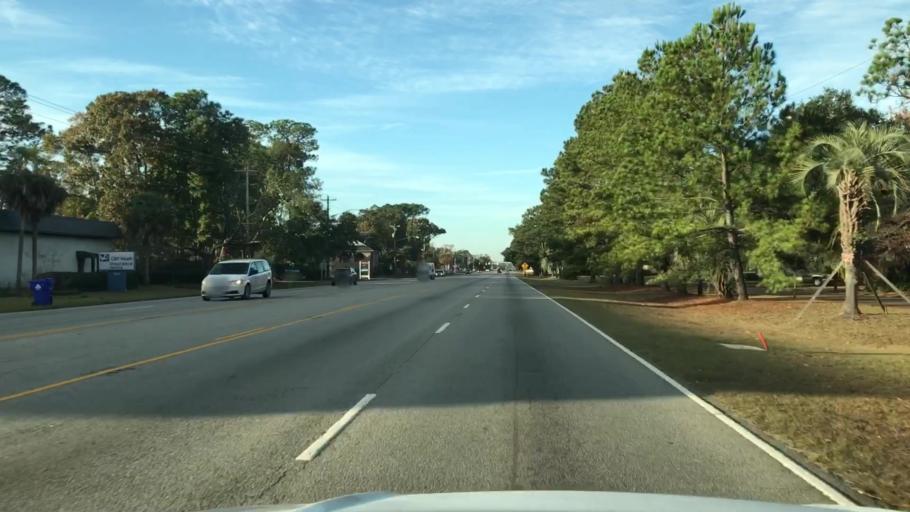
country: US
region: South Carolina
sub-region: Charleston County
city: North Charleston
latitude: 32.8099
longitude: -80.0047
